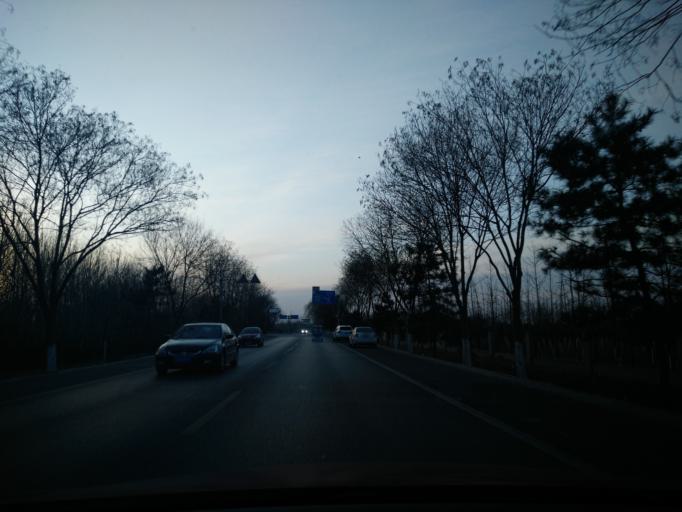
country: CN
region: Beijing
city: Qingyundian
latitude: 39.6730
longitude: 116.5190
